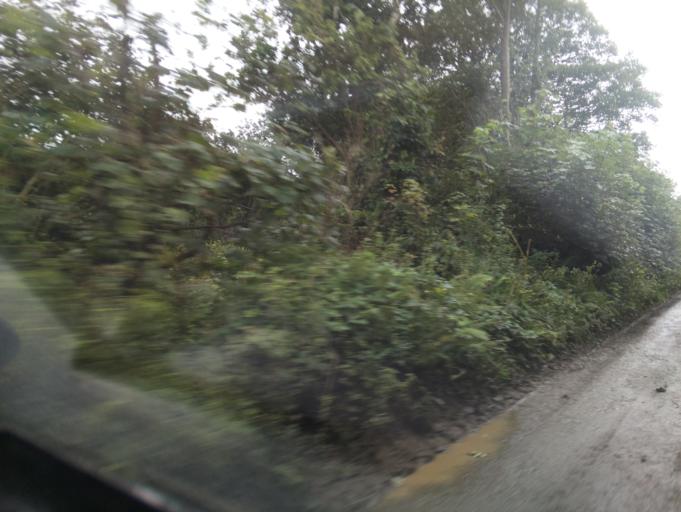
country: GB
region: England
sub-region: Devon
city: Totnes
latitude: 50.3317
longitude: -3.6849
